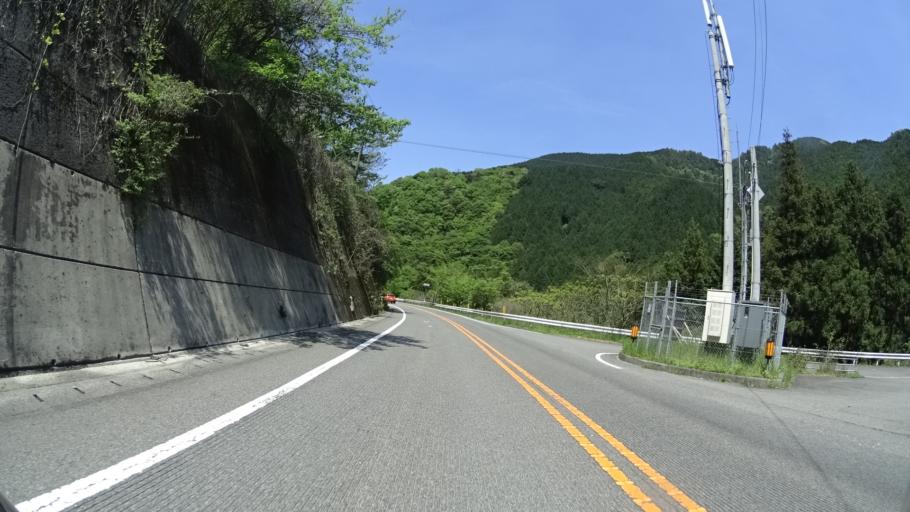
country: JP
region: Ehime
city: Hojo
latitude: 33.9544
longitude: 132.9117
